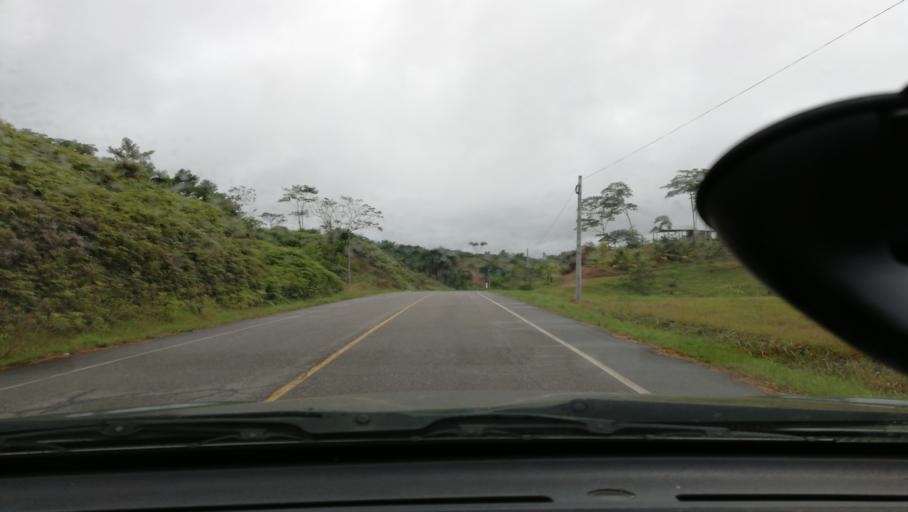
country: PE
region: Loreto
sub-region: Provincia de Loreto
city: Nauta
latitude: -4.4103
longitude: -73.5820
